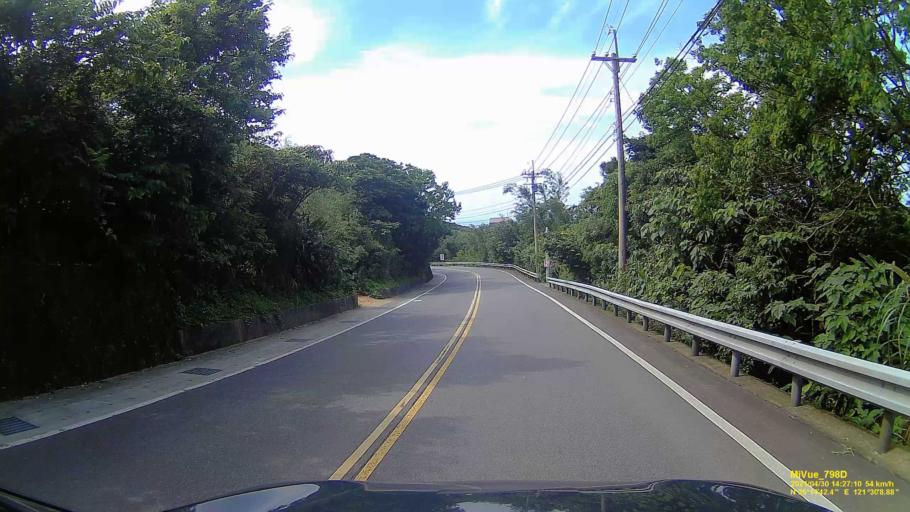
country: TW
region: Taipei
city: Taipei
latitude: 25.2455
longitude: 121.5024
